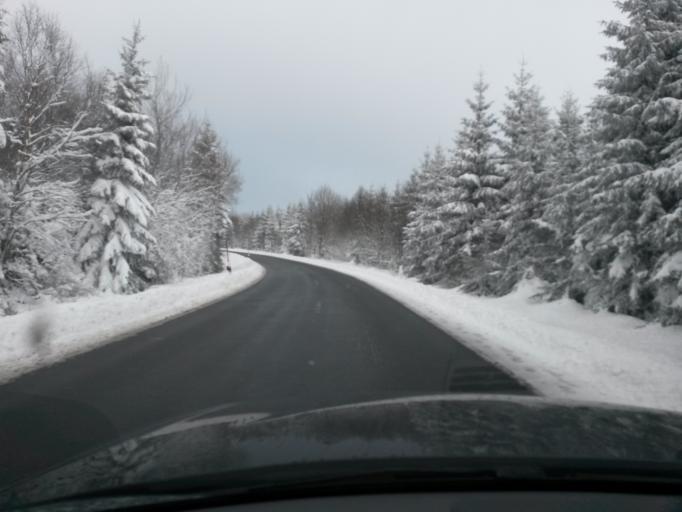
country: DE
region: Bavaria
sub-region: Regierungsbezirk Unterfranken
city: Bischofsheim an der Rhon
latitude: 50.4661
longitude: 9.9893
